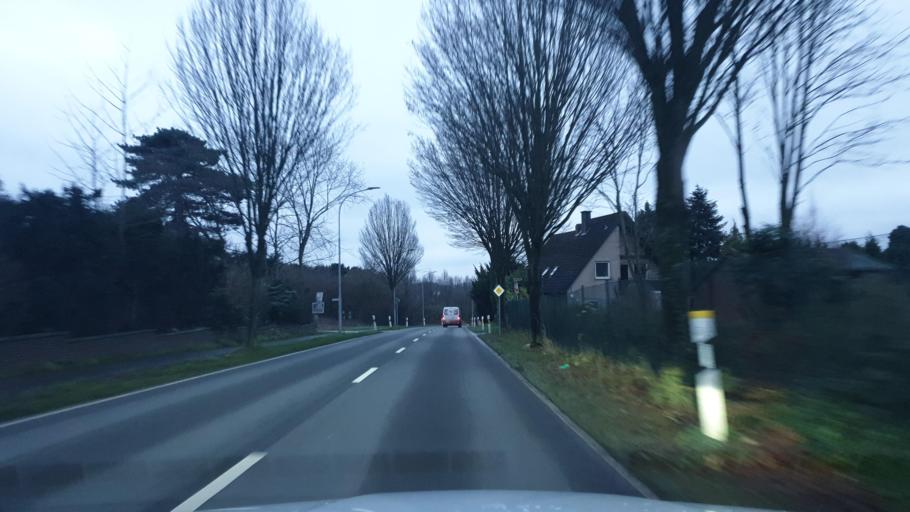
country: DE
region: North Rhine-Westphalia
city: Bad Oeynhausen
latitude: 52.1746
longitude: 8.8144
